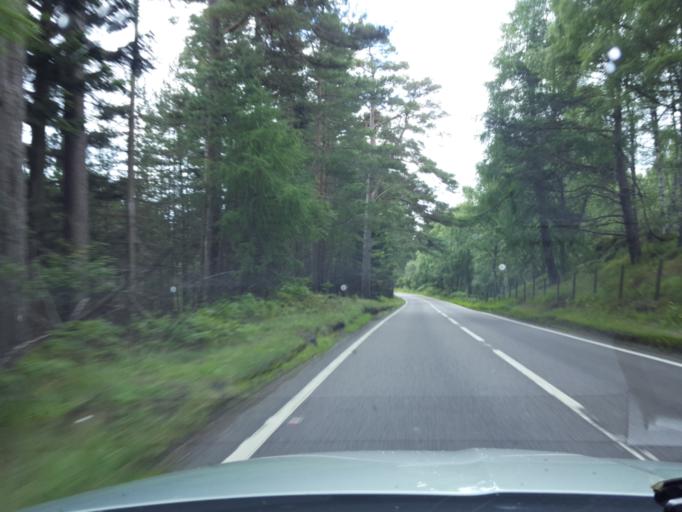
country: GB
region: Scotland
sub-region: Highland
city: Aviemore
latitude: 57.2397
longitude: -3.8054
